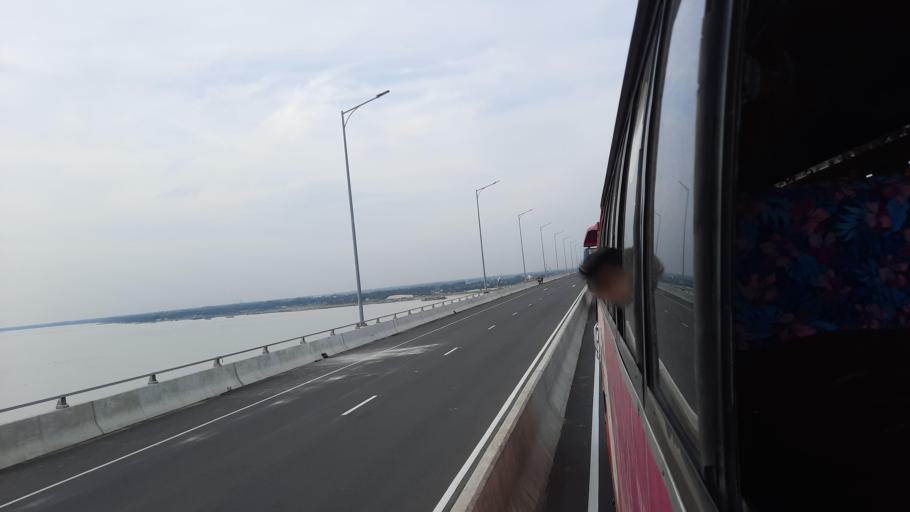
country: BD
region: Dhaka
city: Char Bhadrasan
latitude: 23.4583
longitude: 90.2623
